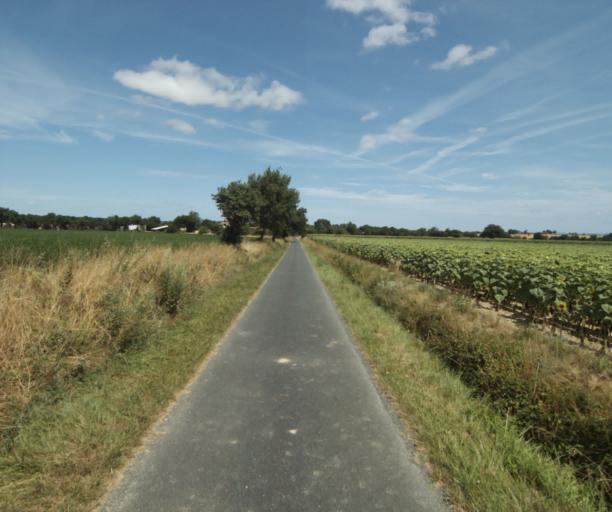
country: FR
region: Midi-Pyrenees
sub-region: Departement du Tarn
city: Soreze
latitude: 43.4990
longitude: 2.0654
